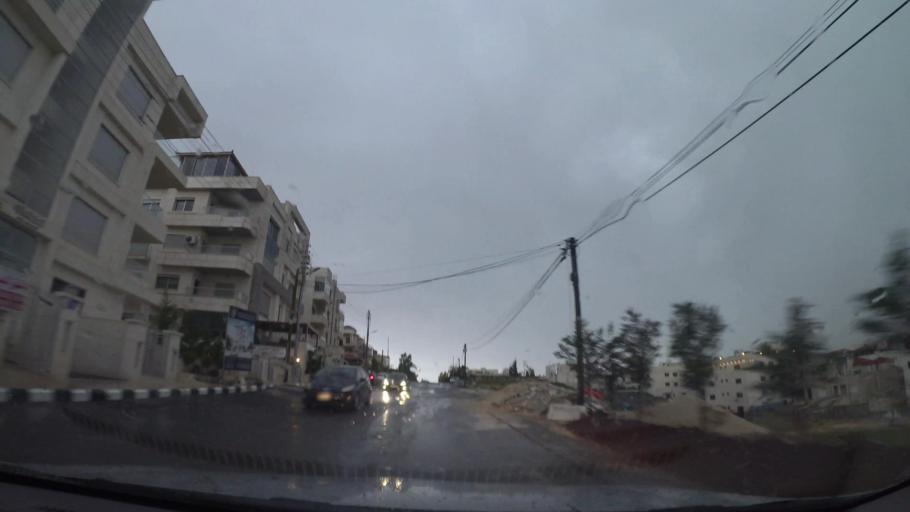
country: JO
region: Amman
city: Umm as Summaq
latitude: 31.9056
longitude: 35.8583
